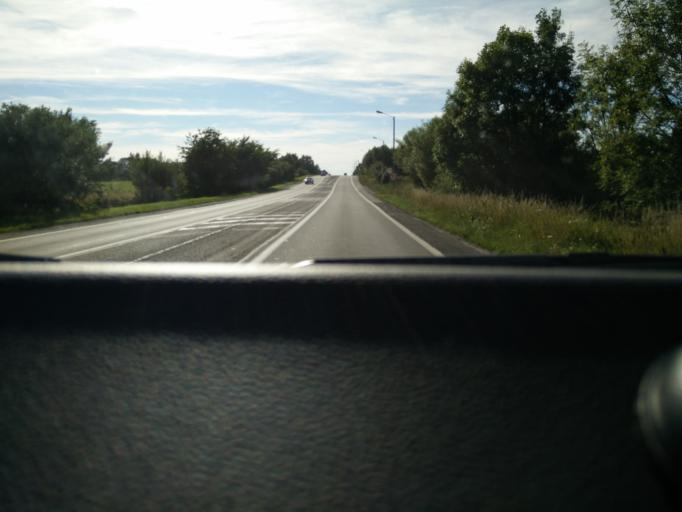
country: FR
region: Nord-Pas-de-Calais
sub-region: Departement du Nord
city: Feignies
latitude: 50.2821
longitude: 3.8934
